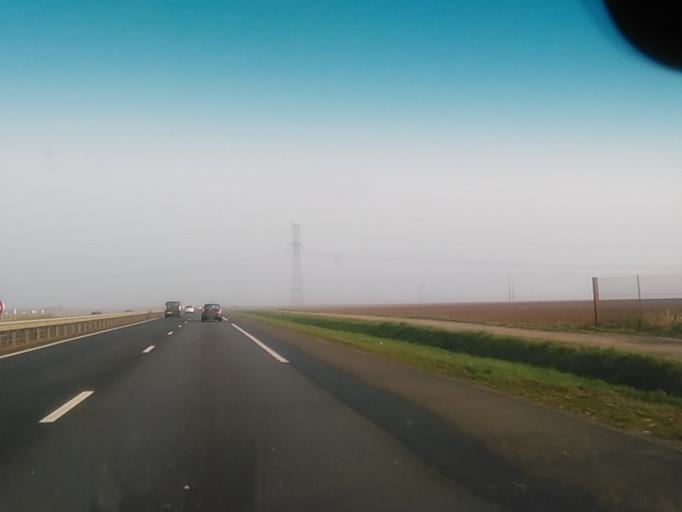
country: FR
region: Lower Normandy
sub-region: Departement du Calvados
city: Bourguebus
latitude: 49.1011
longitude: -0.3132
